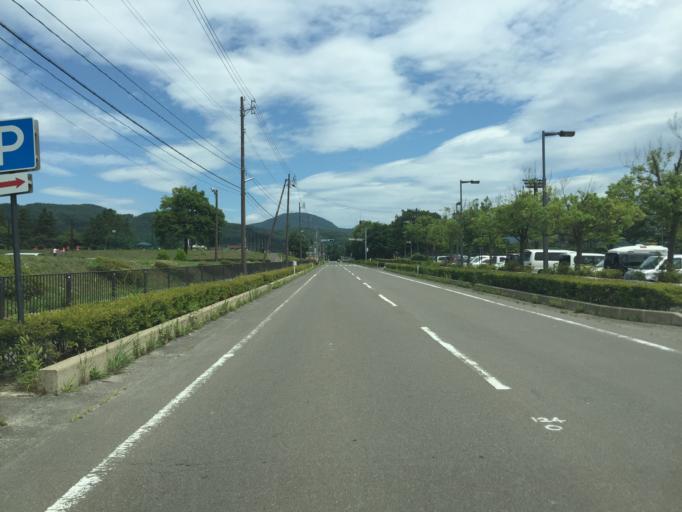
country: JP
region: Fukushima
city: Fukushima-shi
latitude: 37.8152
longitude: 140.4148
